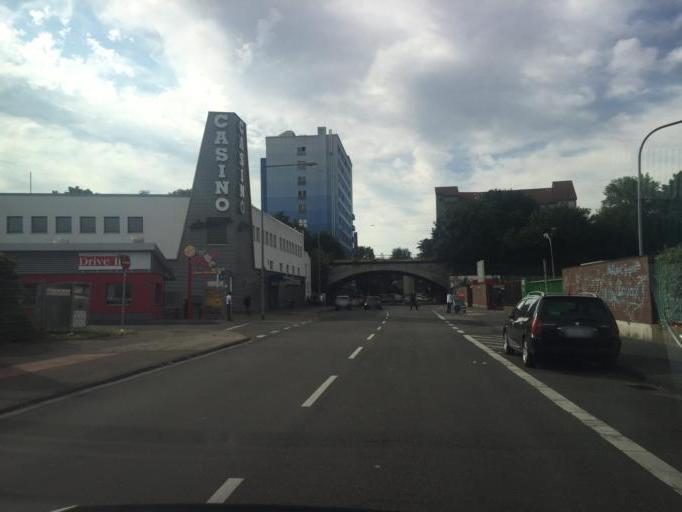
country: DE
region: North Rhine-Westphalia
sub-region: Regierungsbezirk Koln
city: Neuehrenfeld
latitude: 50.9565
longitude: 6.9388
